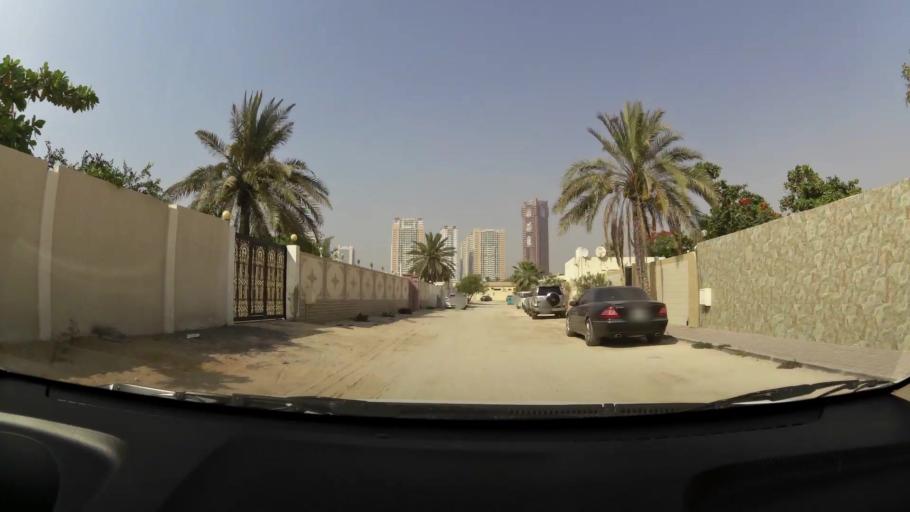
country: AE
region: Ajman
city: Ajman
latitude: 25.3898
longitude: 55.4245
